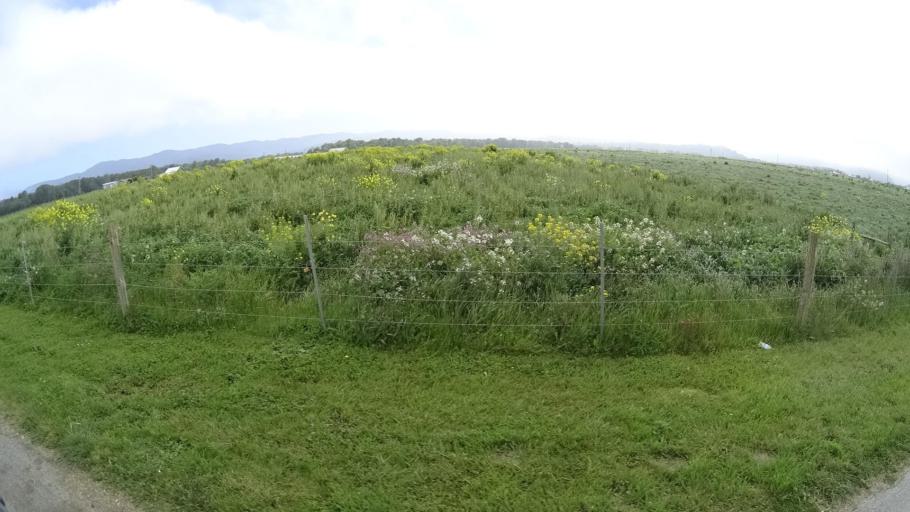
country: US
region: California
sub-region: Humboldt County
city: Fortuna
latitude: 40.5759
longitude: -124.1877
